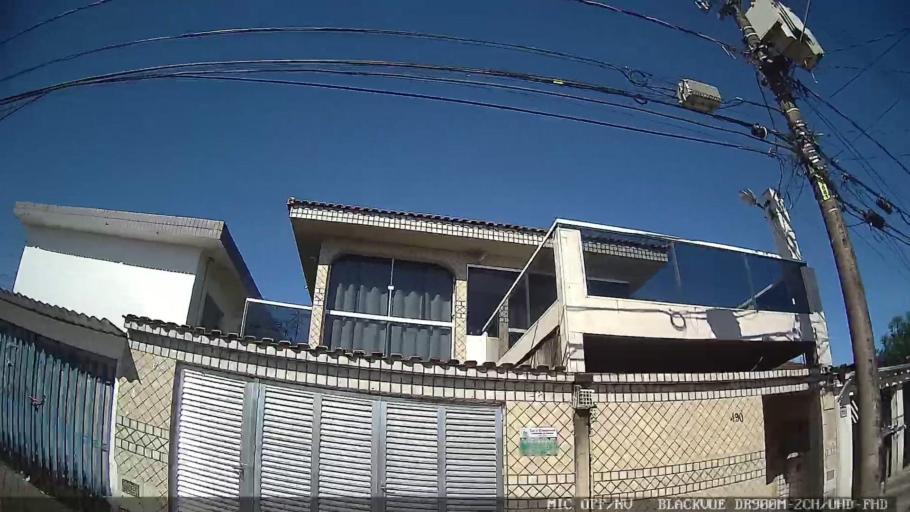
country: BR
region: Sao Paulo
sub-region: Santos
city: Santos
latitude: -23.9400
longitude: -46.2922
